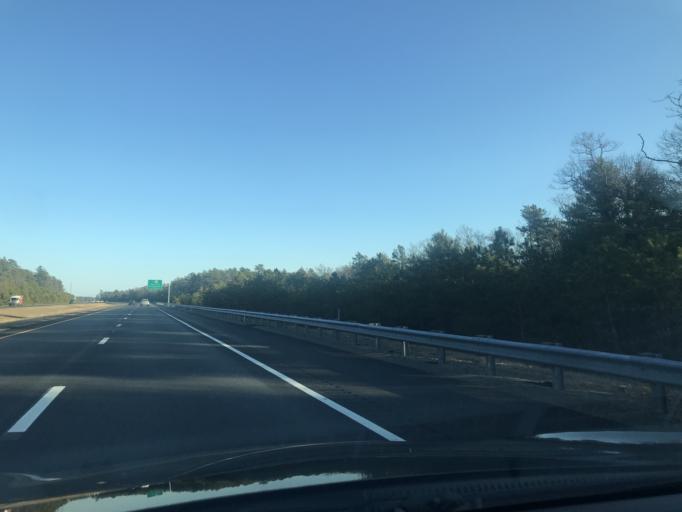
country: US
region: Massachusetts
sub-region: Plymouth County
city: Kingston
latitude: 41.9595
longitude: -70.7284
